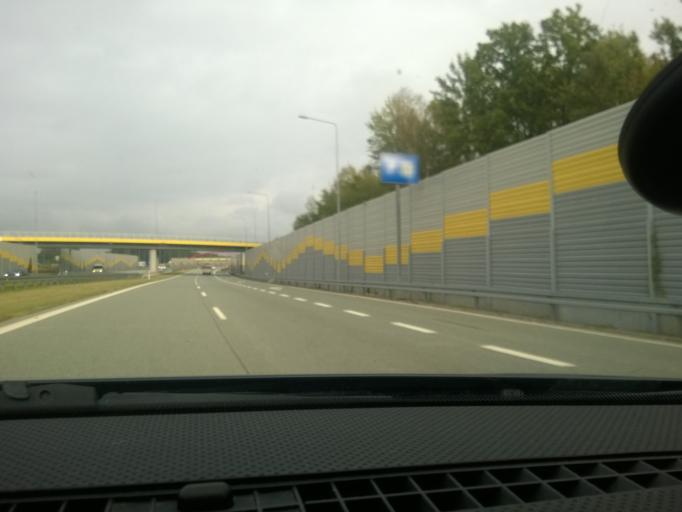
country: PL
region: Lodz Voivodeship
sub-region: Powiat pabianicki
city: Ksawerow
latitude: 51.6331
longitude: 19.4326
